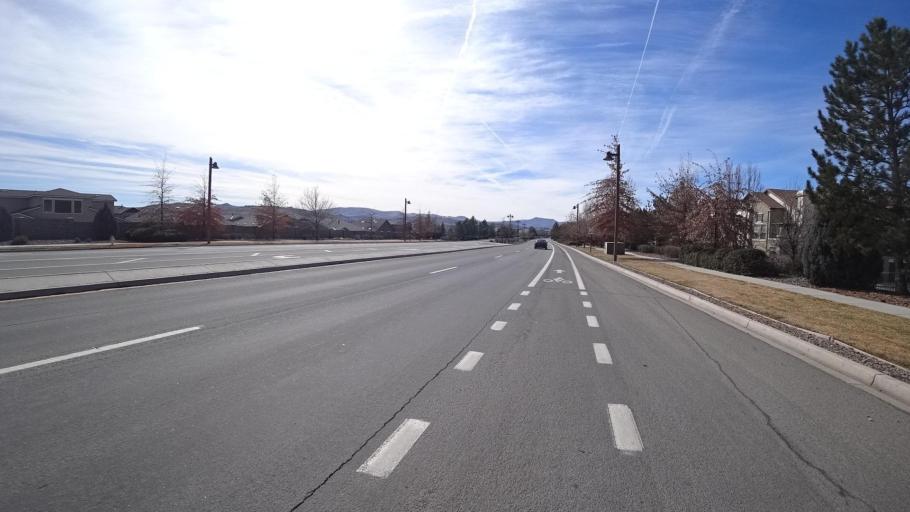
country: US
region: Nevada
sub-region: Washoe County
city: Sun Valley
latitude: 39.6038
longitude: -119.7297
